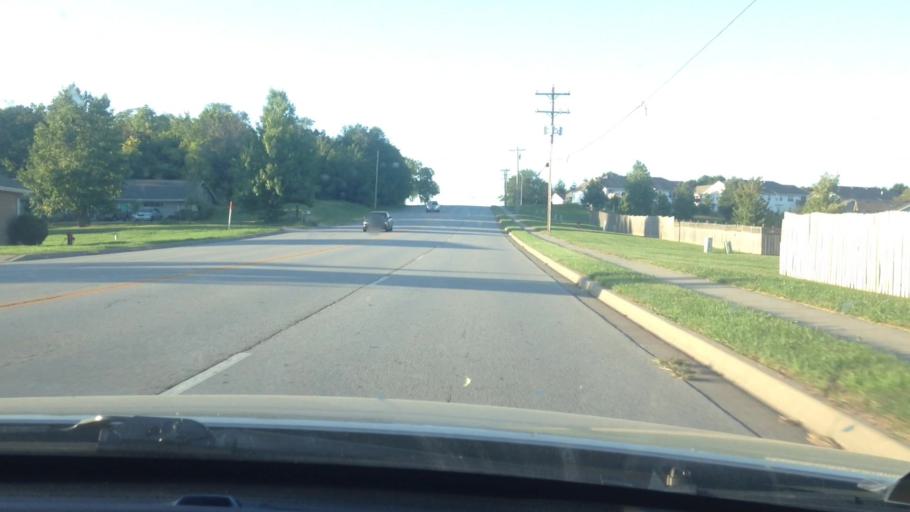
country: US
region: Missouri
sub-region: Platte County
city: Platte City
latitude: 39.3410
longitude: -94.7613
